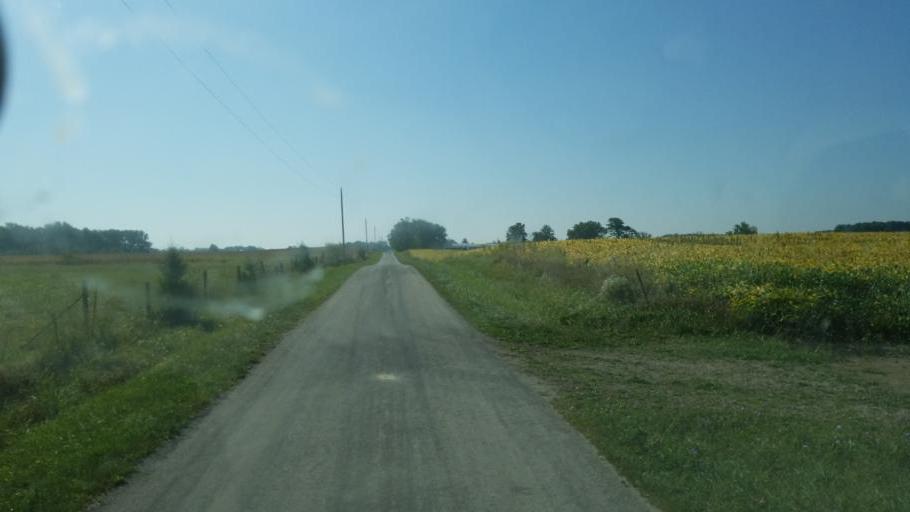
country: US
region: Ohio
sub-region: Union County
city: Richwood
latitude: 40.5342
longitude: -83.4117
